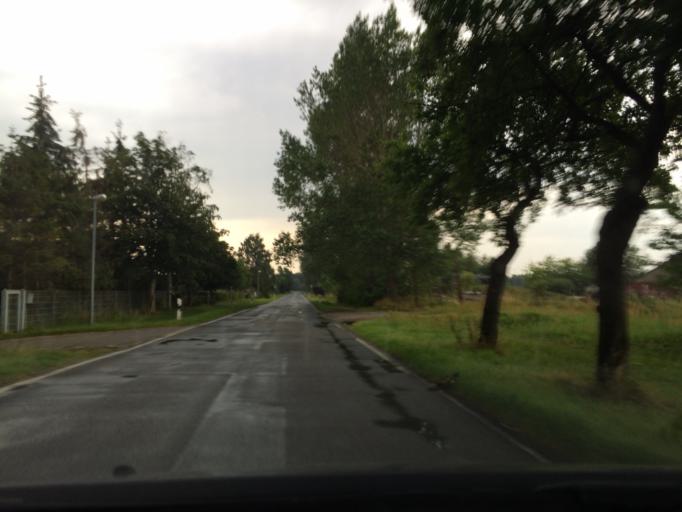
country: DE
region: Mecklenburg-Vorpommern
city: Altenpleen
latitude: 54.3629
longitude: 12.9367
